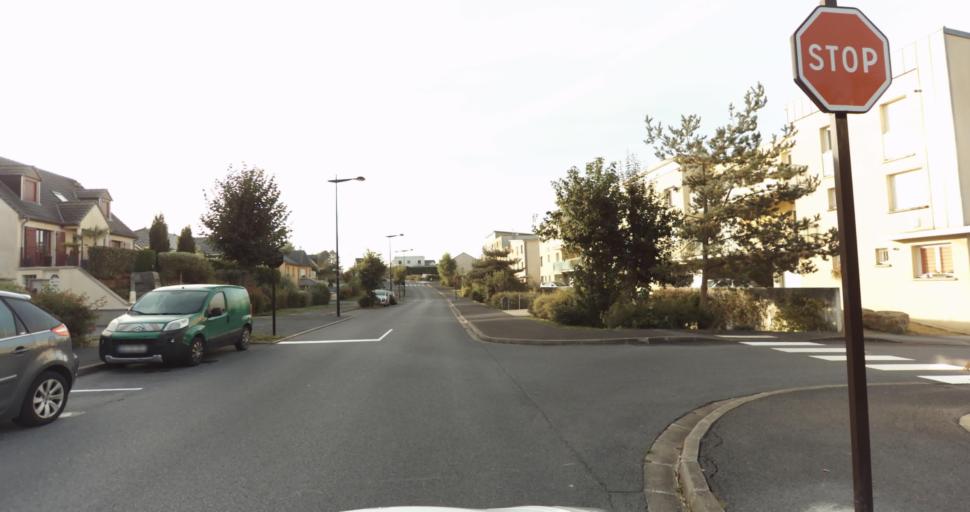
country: FR
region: Champagne-Ardenne
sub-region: Departement des Ardennes
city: Villers-Semeuse
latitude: 49.7390
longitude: 4.7421
